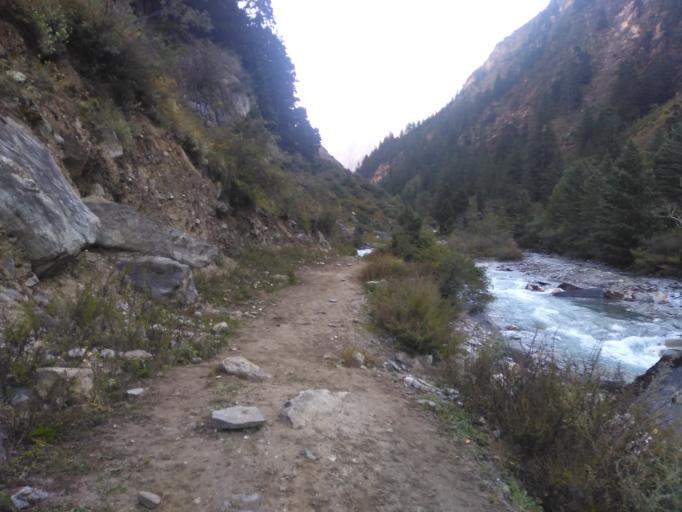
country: NP
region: Western Region
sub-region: Dhawalagiri Zone
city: Jomsom
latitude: 28.9266
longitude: 83.0389
